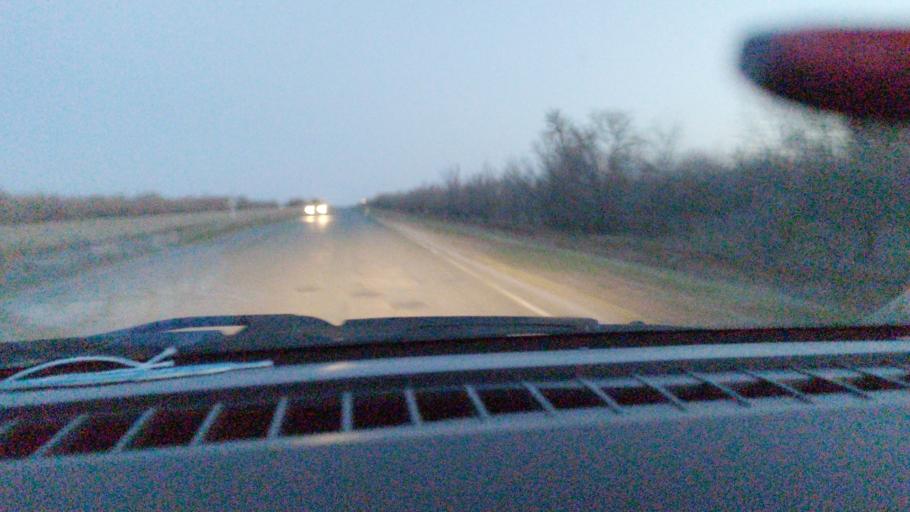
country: RU
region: Saratov
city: Rovnoye
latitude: 50.9760
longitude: 46.1172
